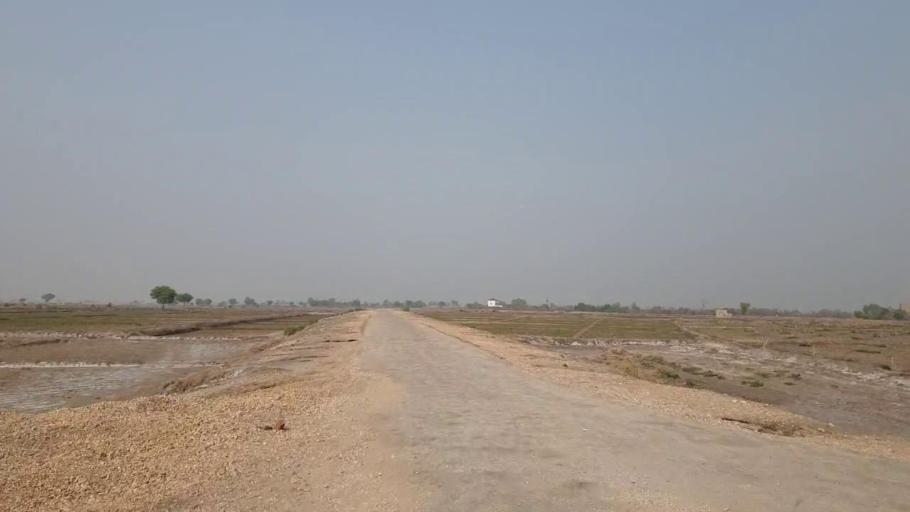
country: PK
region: Sindh
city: Bhan
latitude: 26.4853
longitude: 67.7008
